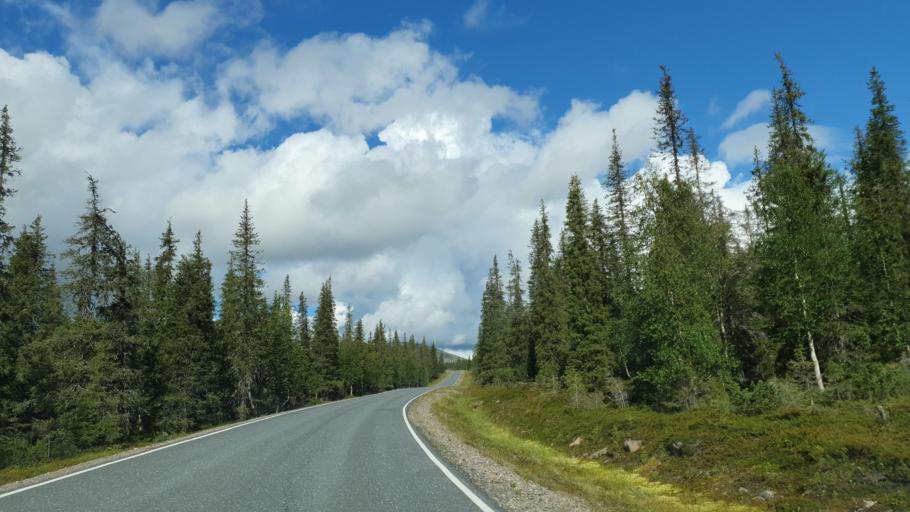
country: FI
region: Lapland
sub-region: Tunturi-Lappi
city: Muonio
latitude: 68.0371
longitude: 24.0659
